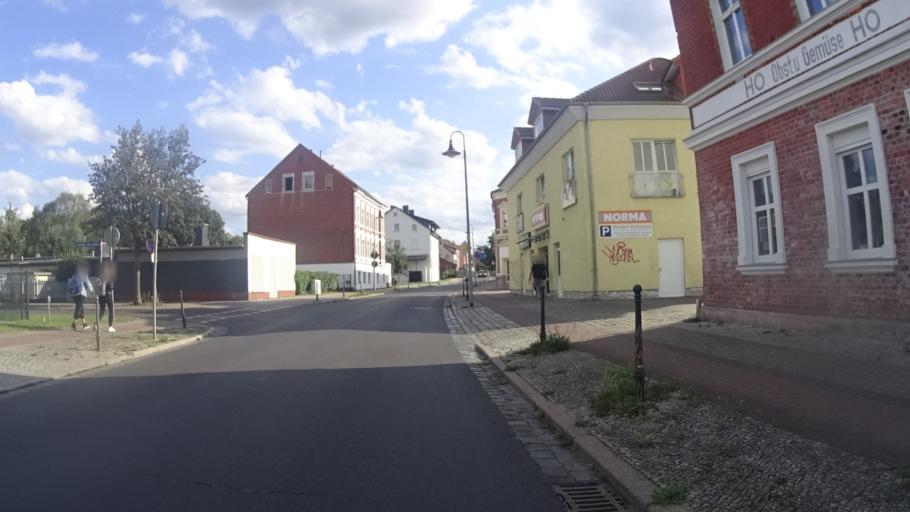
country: DE
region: Brandenburg
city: Rathenow
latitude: 52.6116
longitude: 12.3337
